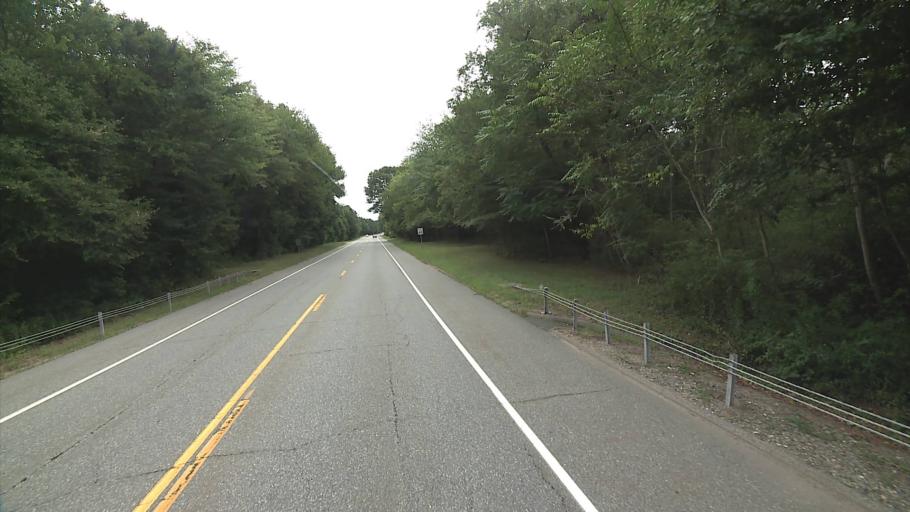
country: US
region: Connecticut
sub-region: Middlesex County
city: Old Saybrook Center
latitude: 41.3099
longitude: -72.3338
